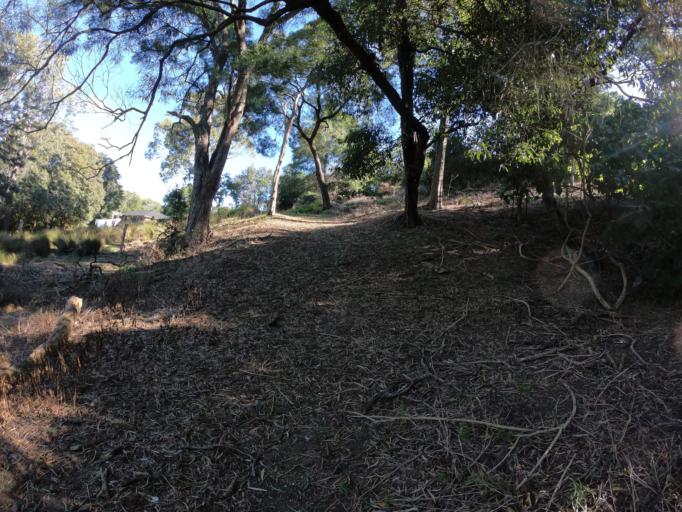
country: AU
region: New South Wales
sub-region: Wollongong
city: Mount Keira
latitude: -34.4136
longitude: 150.8529
